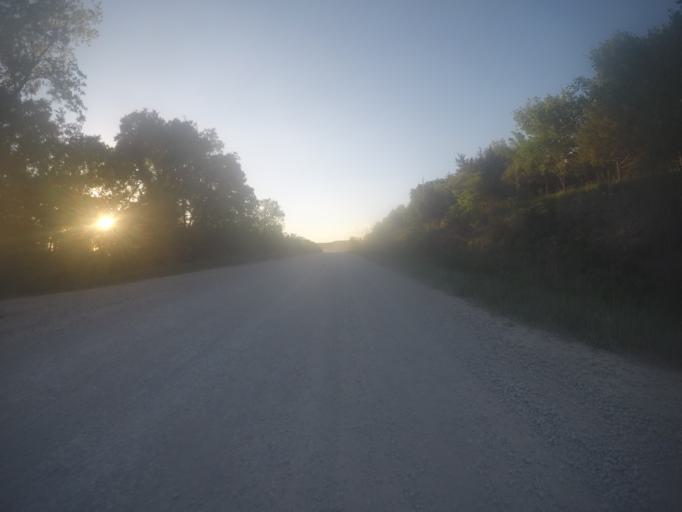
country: US
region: Kansas
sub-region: Riley County
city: Manhattan
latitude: 39.2375
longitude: -96.5572
